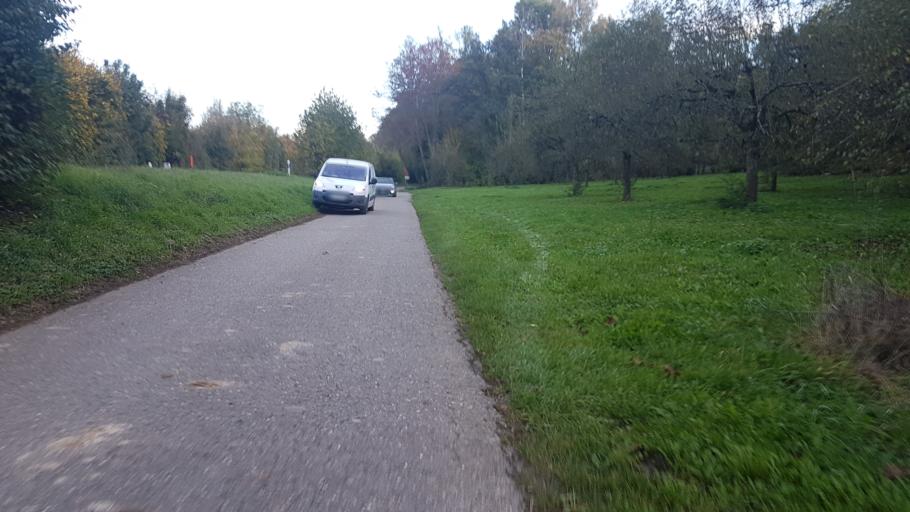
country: DE
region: Baden-Wuerttemberg
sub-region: Karlsruhe Region
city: Neckarzimmern
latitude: 49.3231
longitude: 9.1085
